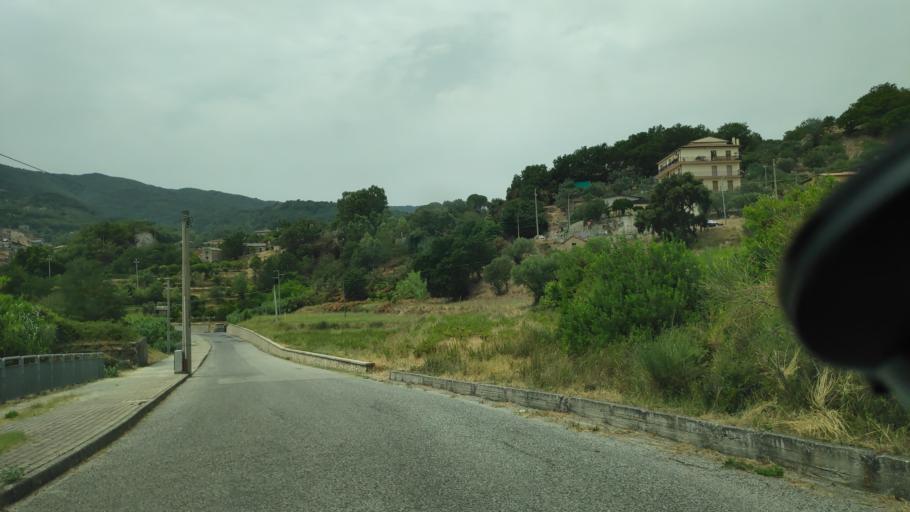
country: IT
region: Calabria
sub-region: Provincia di Catanzaro
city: Davoli
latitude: 38.6557
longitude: 16.4908
